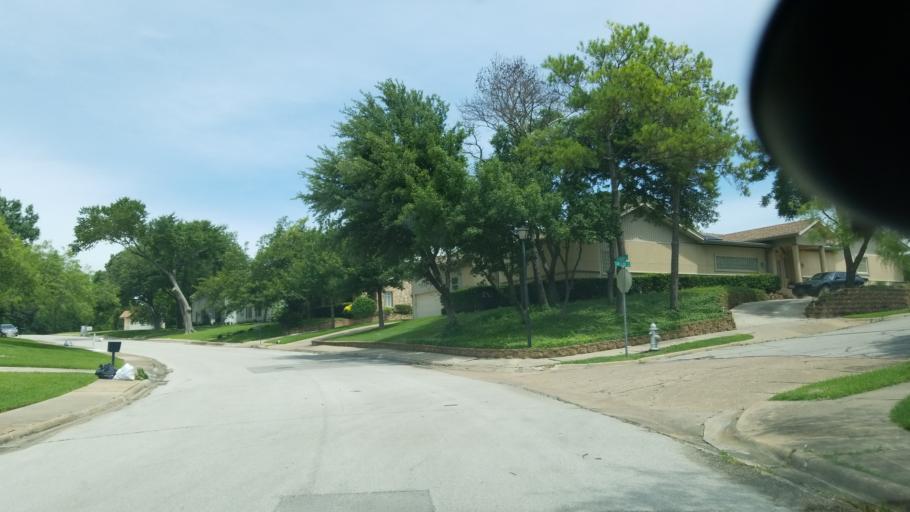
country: US
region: Texas
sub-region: Dallas County
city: Irving
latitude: 32.8456
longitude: -96.9401
